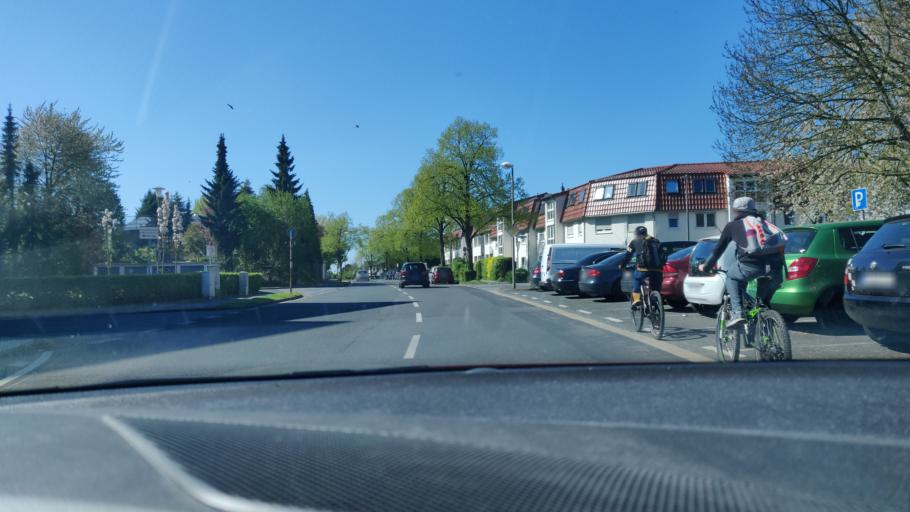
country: DE
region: North Rhine-Westphalia
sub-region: Regierungsbezirk Dusseldorf
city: Mettmann
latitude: 51.2565
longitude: 6.9630
